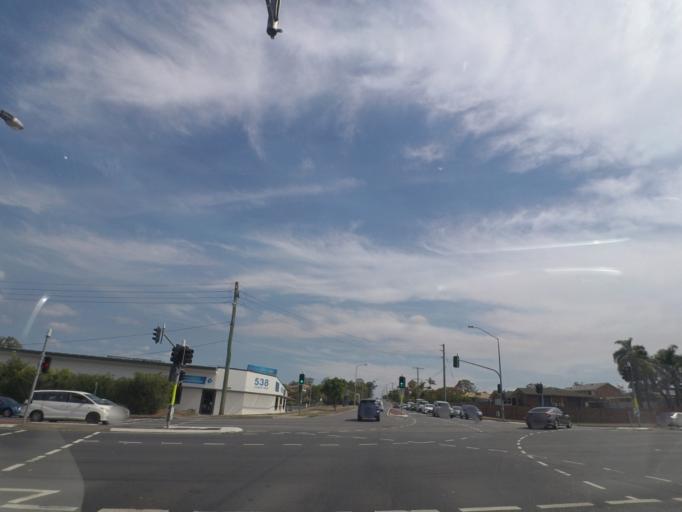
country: AU
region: Queensland
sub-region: Brisbane
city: Sunnybank Hills
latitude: -27.6112
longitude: 153.0621
